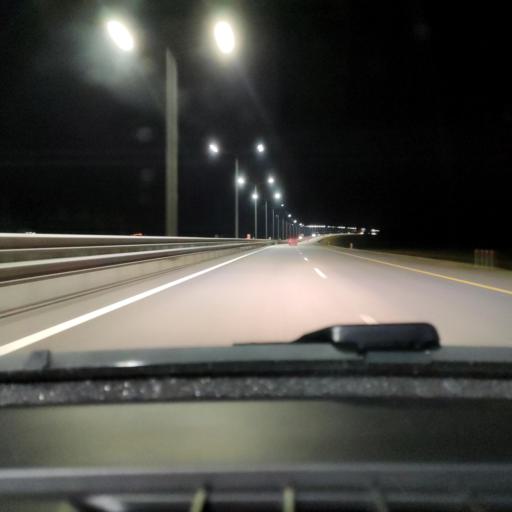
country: RU
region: Voronezj
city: Podkletnoye
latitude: 51.5321
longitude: 39.5080
